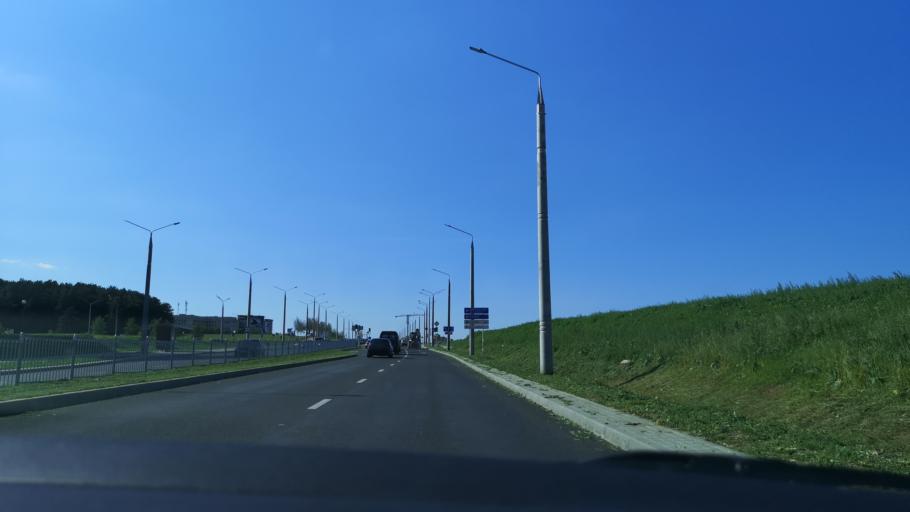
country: BY
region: Grodnenskaya
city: Hrodna
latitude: 53.6465
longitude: 23.8683
